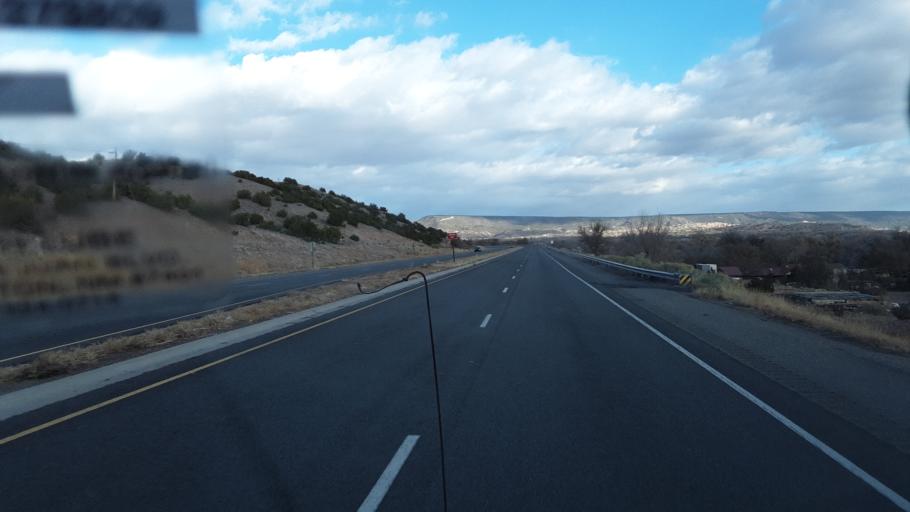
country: US
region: New Mexico
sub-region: Rio Arriba County
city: Ohkay Owingeh
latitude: 36.0304
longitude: -106.0934
